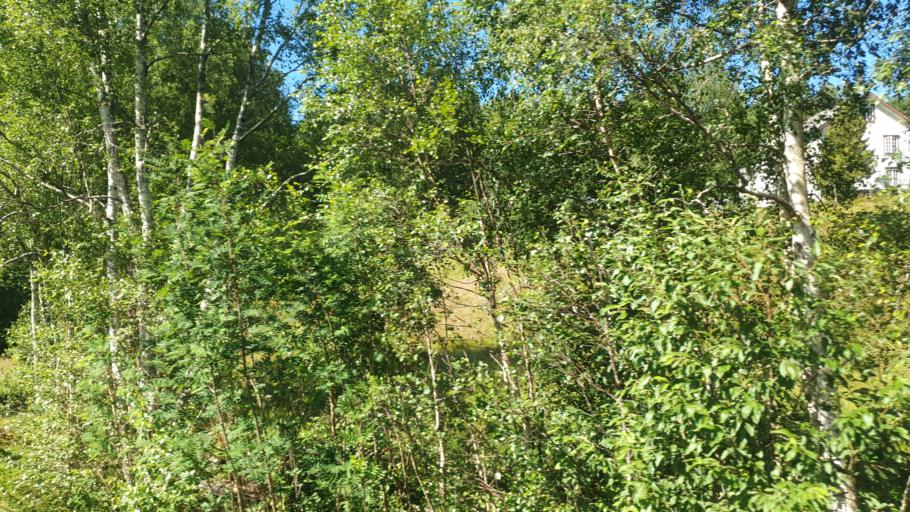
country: NO
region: Sor-Trondelag
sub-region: Meldal
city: Meldal
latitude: 63.1300
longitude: 9.7070
